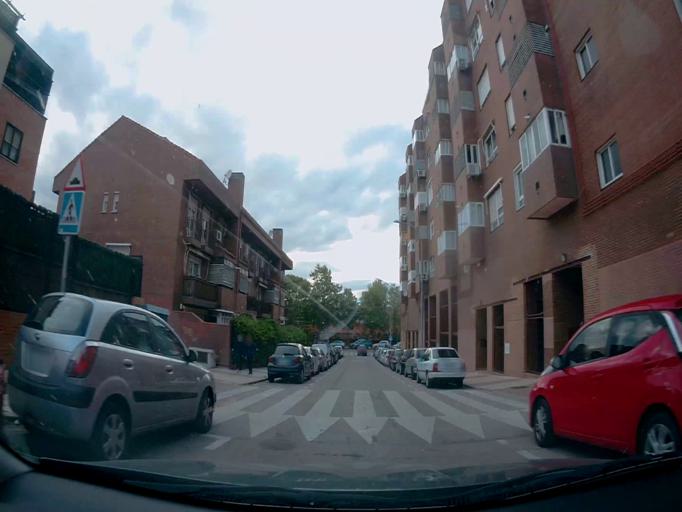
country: ES
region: Madrid
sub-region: Provincia de Madrid
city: Alcorcon
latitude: 40.3389
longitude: -3.8373
